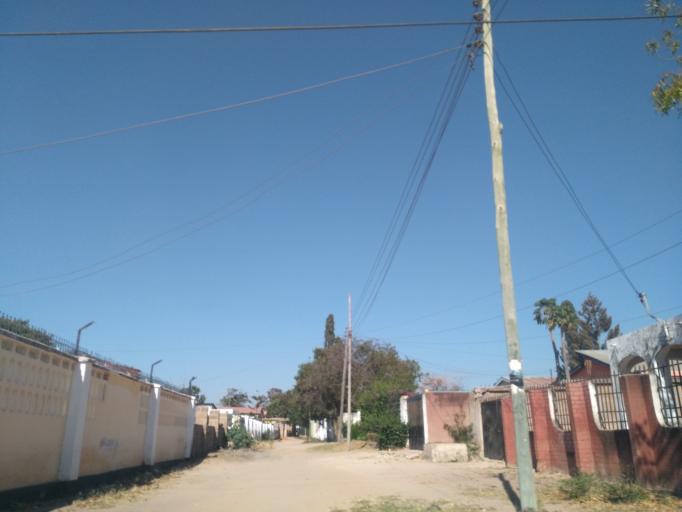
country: TZ
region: Dodoma
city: Dodoma
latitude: -6.1604
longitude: 35.7506
